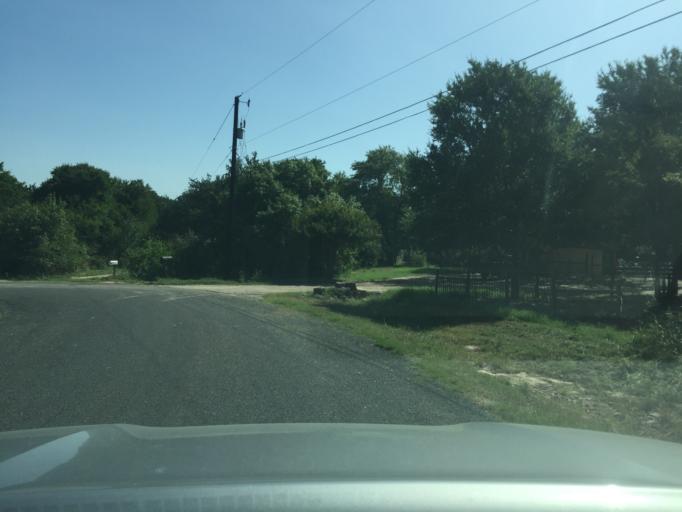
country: US
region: Texas
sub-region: Bexar County
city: Timberwood Park
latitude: 29.7125
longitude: -98.4693
